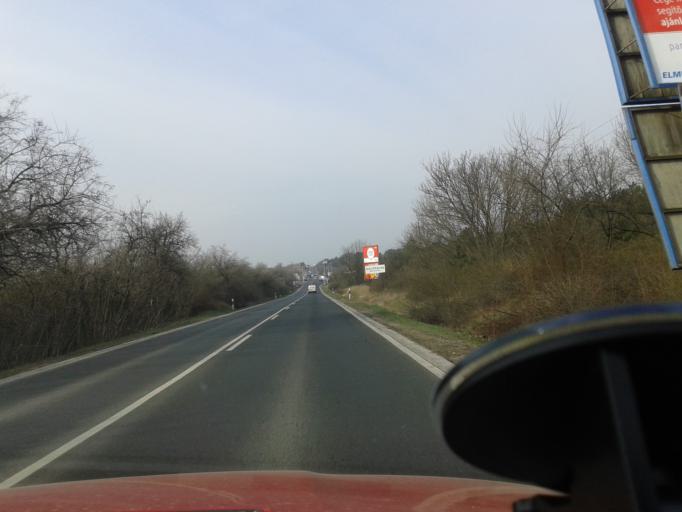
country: HU
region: Pest
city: Diosd
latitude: 47.4209
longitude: 18.9887
